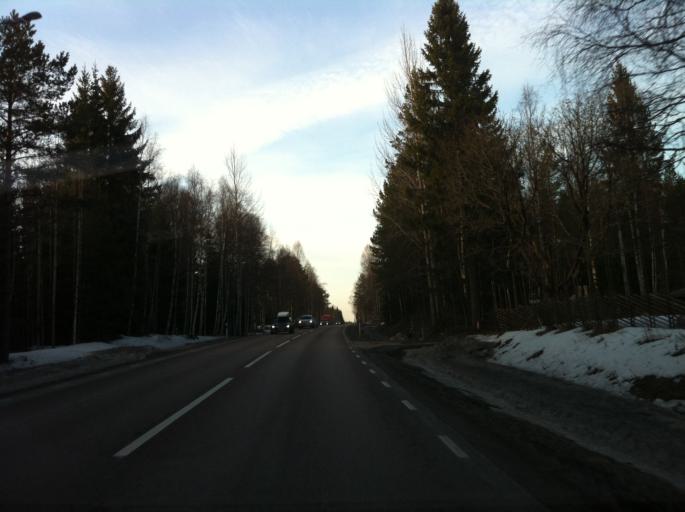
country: SE
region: Vaermland
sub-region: Filipstads Kommun
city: Lesjofors
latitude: 59.9925
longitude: 14.1673
